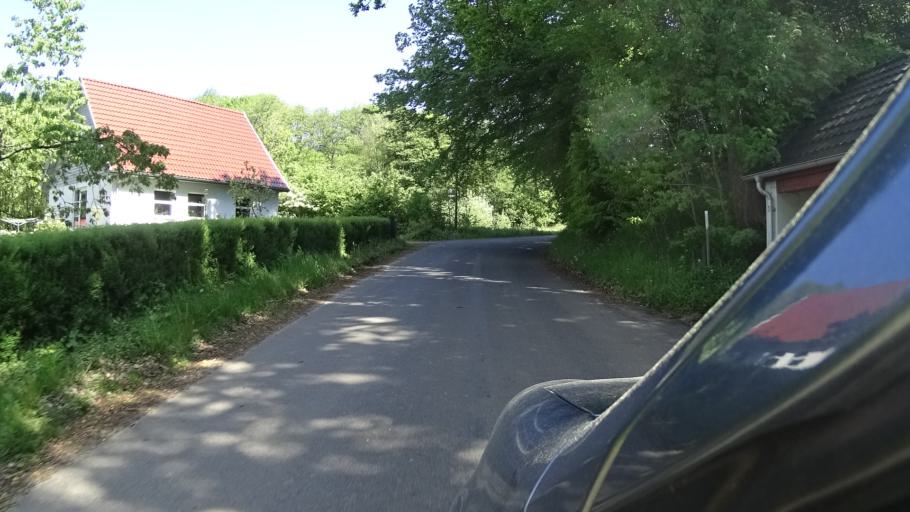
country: DK
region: South Denmark
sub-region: Vejle Kommune
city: Borkop
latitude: 55.6194
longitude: 9.6662
